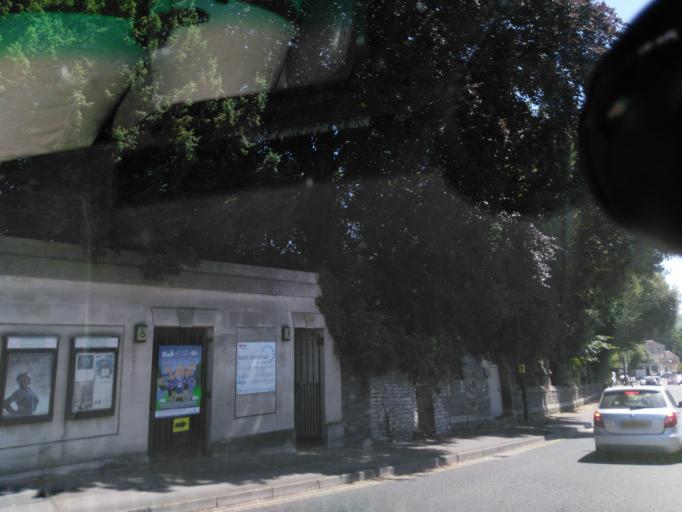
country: GB
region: England
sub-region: Bath and North East Somerset
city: Bath
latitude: 51.3845
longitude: -2.3865
